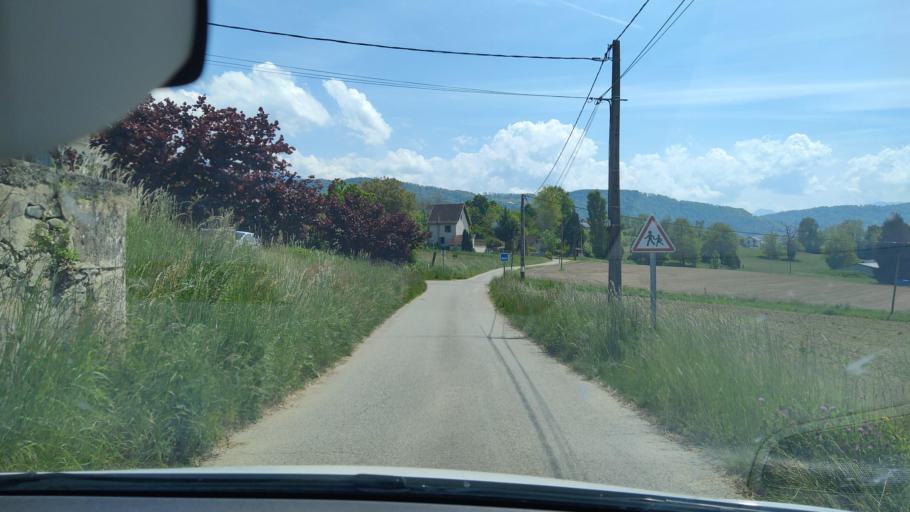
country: FR
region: Rhone-Alpes
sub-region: Departement de la Savoie
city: Domessin
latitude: 45.5239
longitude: 5.7153
